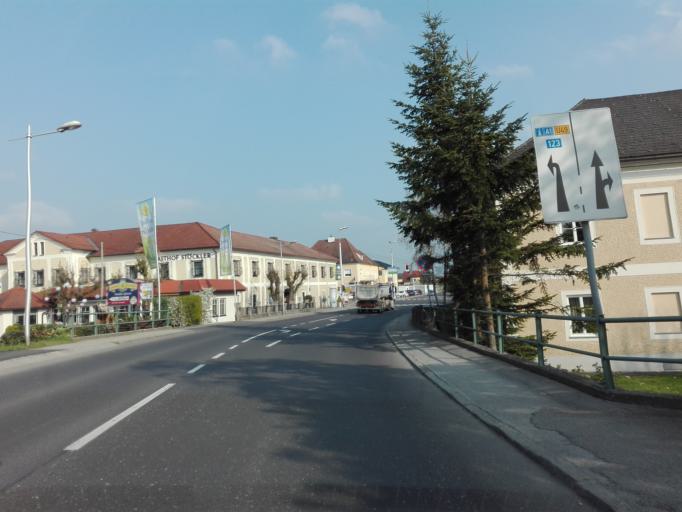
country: AT
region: Upper Austria
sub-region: Politischer Bezirk Linz-Land
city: Enns
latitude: 48.2128
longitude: 14.4881
